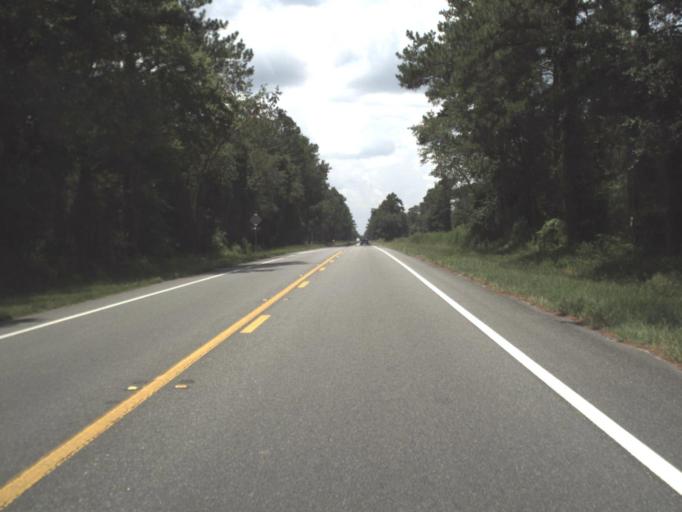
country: US
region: Florida
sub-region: Columbia County
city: Five Points
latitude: 30.2589
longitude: -82.6842
